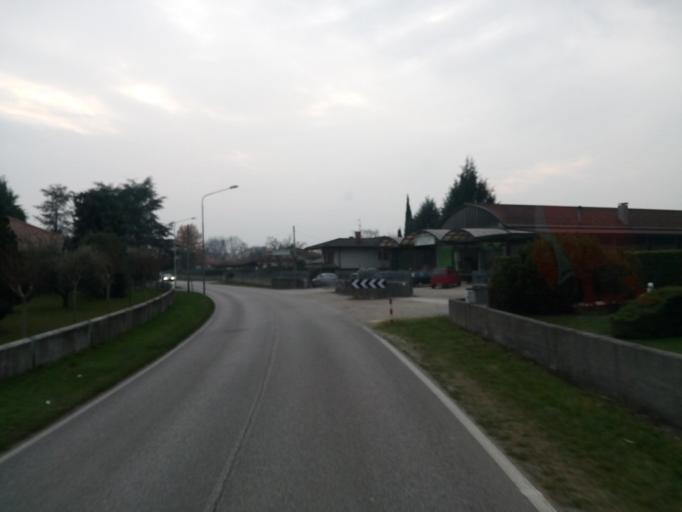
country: IT
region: Friuli Venezia Giulia
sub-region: Provincia di Udine
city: Povoletto
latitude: 46.1216
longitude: 13.3048
